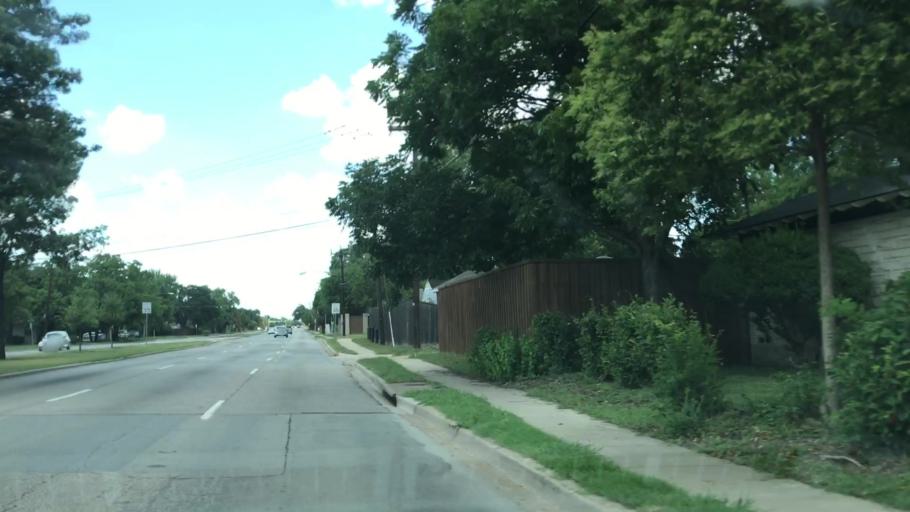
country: US
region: Texas
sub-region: Dallas County
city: University Park
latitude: 32.8741
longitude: -96.8561
